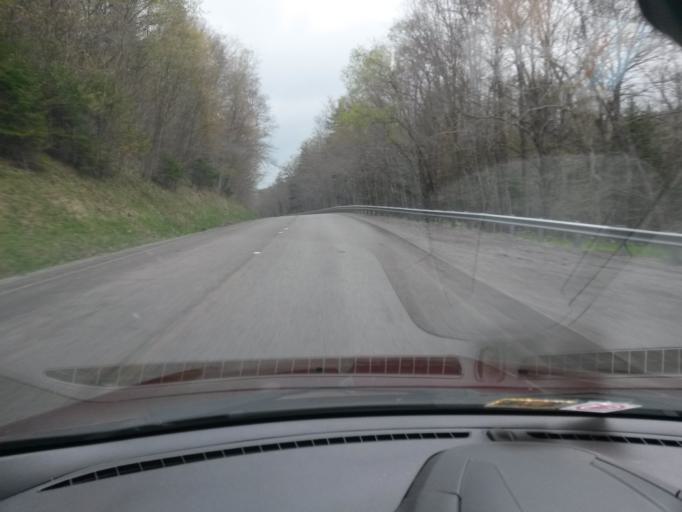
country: US
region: West Virginia
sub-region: Randolph County
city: Elkins
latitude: 38.6274
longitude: -79.9010
